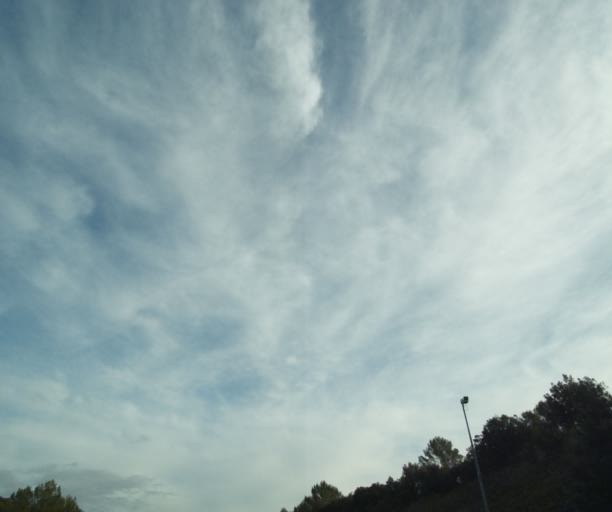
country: FR
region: Provence-Alpes-Cote d'Azur
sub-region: Departement du Var
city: Cabasse
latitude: 43.4007
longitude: 6.2190
